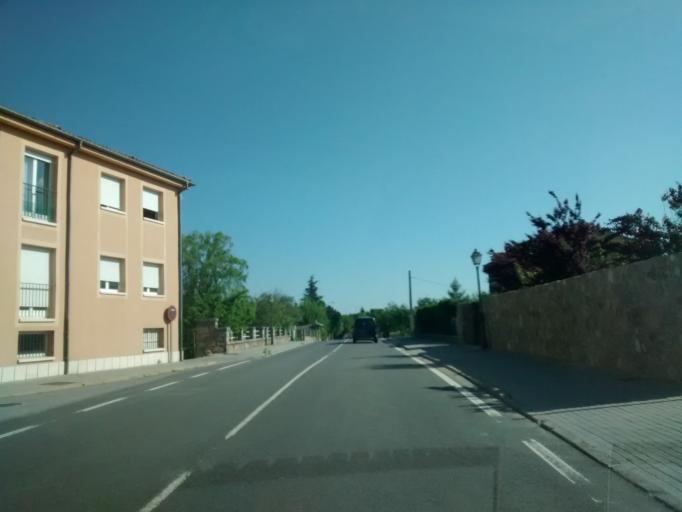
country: ES
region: Castille and Leon
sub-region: Provincia de Segovia
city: Torrecaballeros
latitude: 40.9920
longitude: -4.0228
